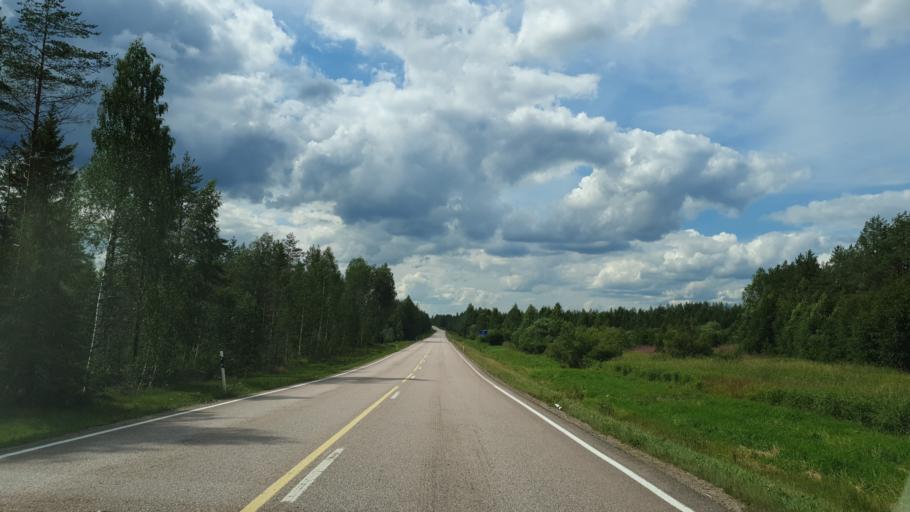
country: FI
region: Kainuu
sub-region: Kehys-Kainuu
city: Hyrynsalmi
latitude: 64.4489
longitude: 28.6225
